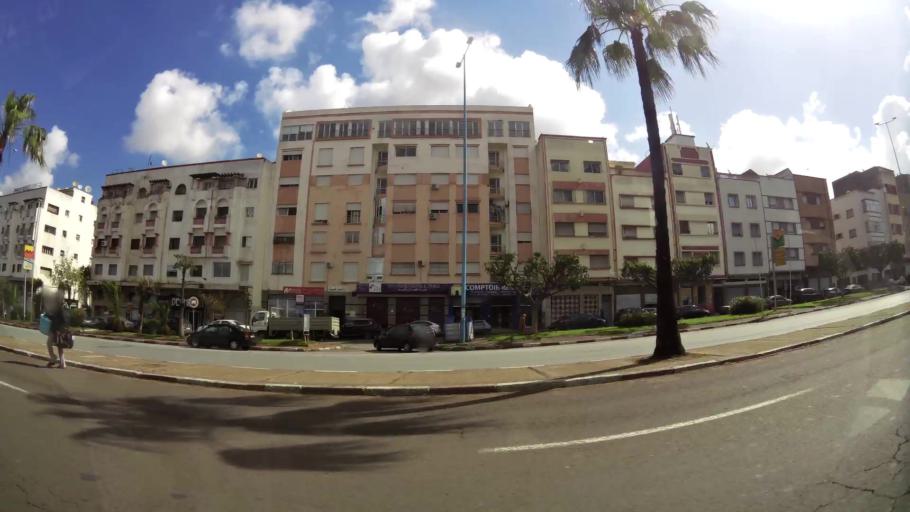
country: MA
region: Grand Casablanca
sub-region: Casablanca
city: Casablanca
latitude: 33.5525
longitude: -7.5903
